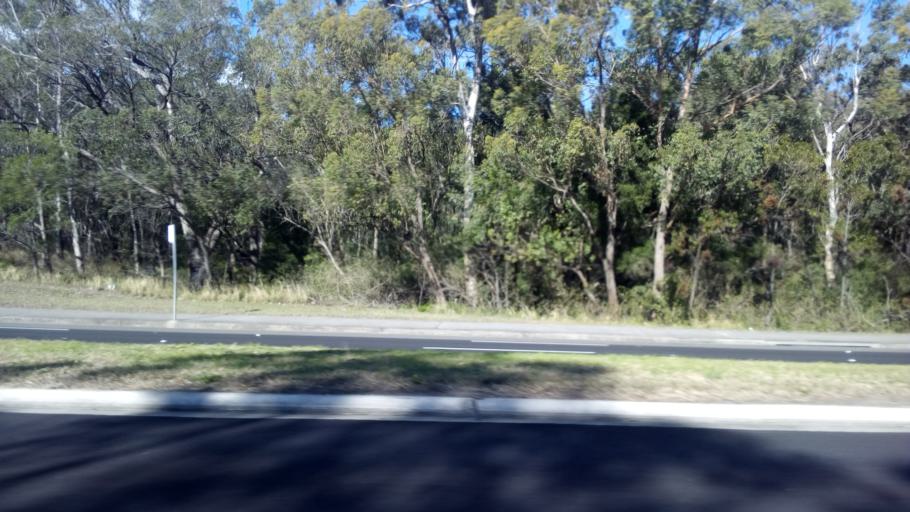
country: AU
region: New South Wales
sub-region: Shellharbour
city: Barrack Heights
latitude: -34.5658
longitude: 150.8262
